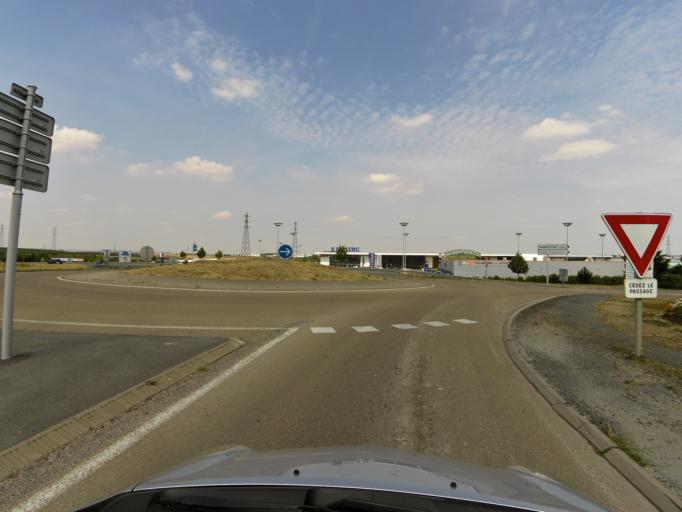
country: FR
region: Champagne-Ardenne
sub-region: Departement de la Marne
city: Bezannes
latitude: 49.2016
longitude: 4.0133
